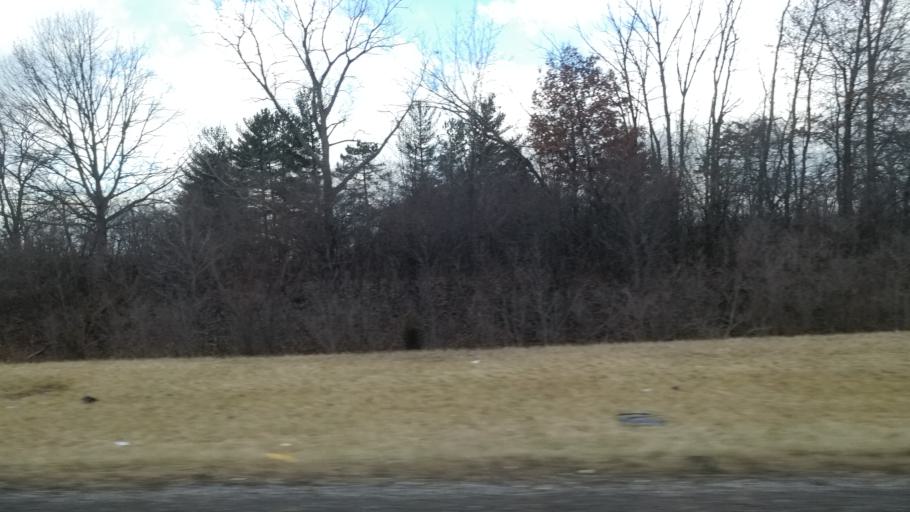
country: US
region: Ohio
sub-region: Lucas County
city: Maumee
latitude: 41.5458
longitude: -83.6969
